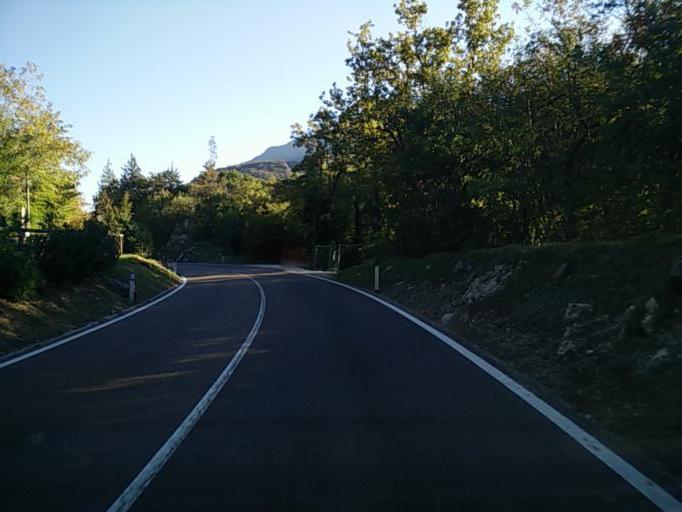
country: IT
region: Trentino-Alto Adige
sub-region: Provincia di Trento
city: Nago-Torbole
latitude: 45.8749
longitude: 10.9054
